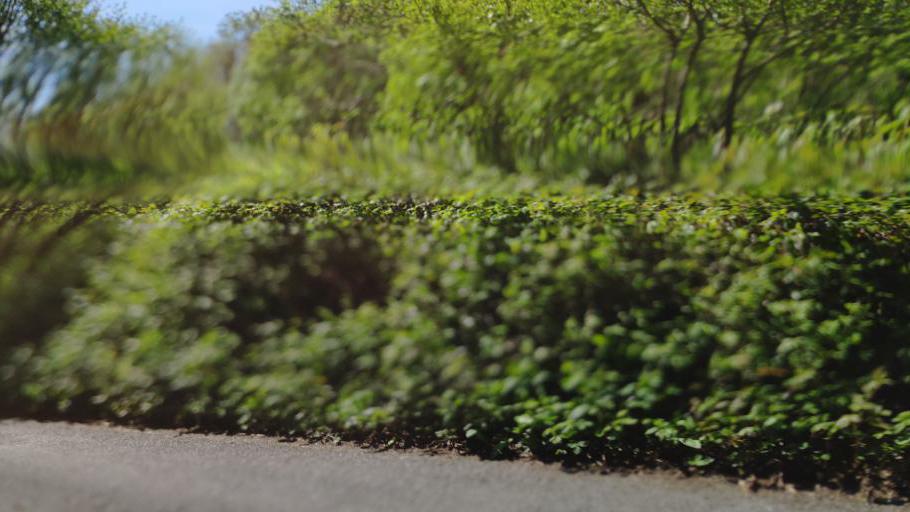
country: IE
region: Munster
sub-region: County Cork
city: Blarney
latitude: 51.9750
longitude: -8.5831
